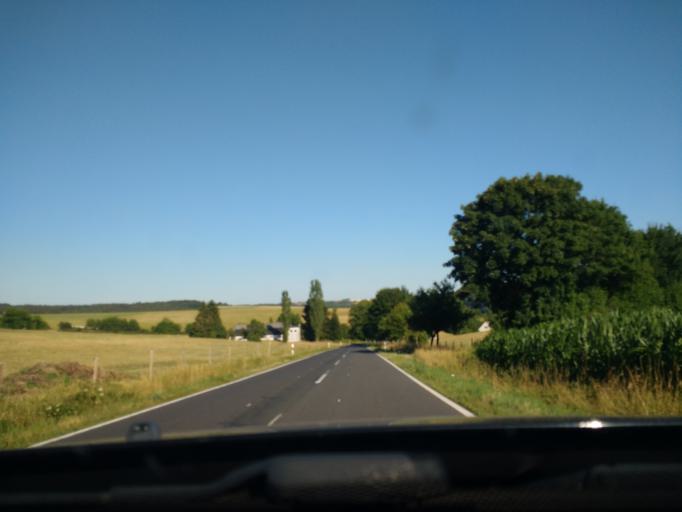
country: DE
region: Rheinland-Pfalz
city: Meisburg
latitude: 50.1081
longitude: 6.6989
